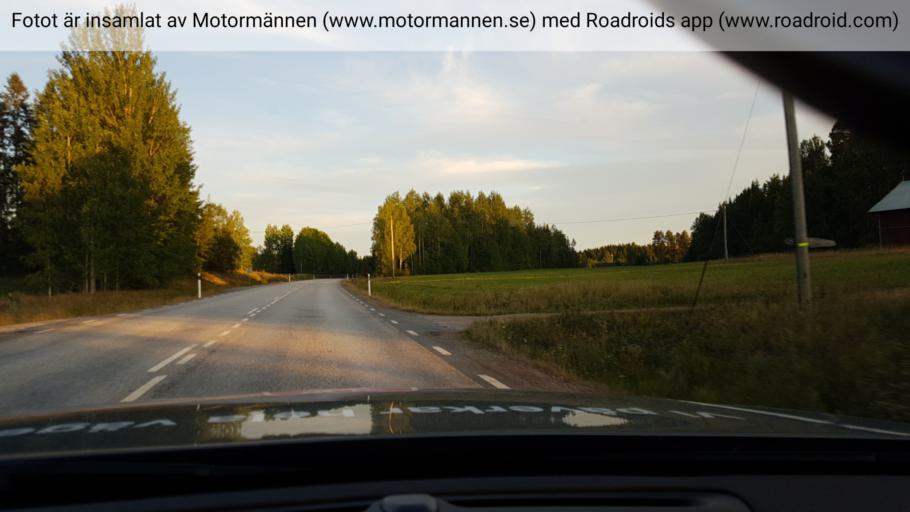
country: SE
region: Vaermland
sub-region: Storfors Kommun
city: Storfors
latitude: 59.4963
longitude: 14.3250
